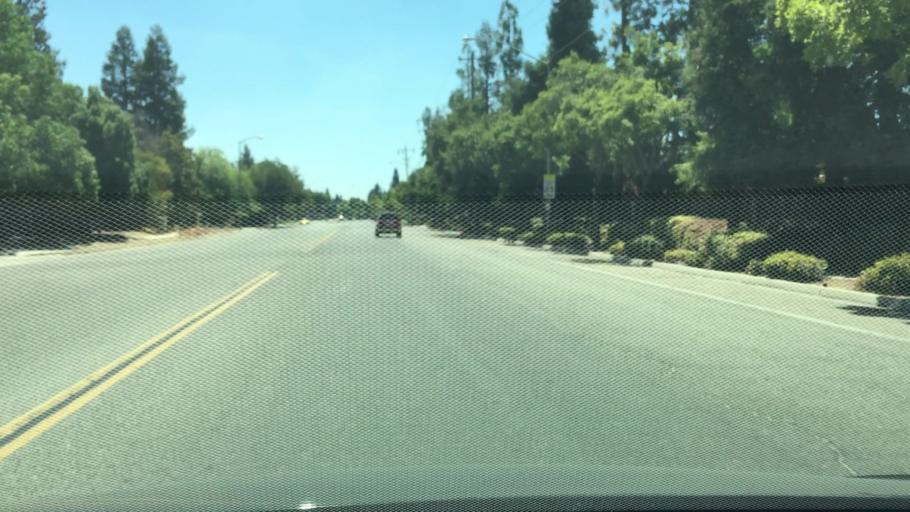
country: US
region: California
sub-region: Fresno County
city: Clovis
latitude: 36.8479
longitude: -119.7476
